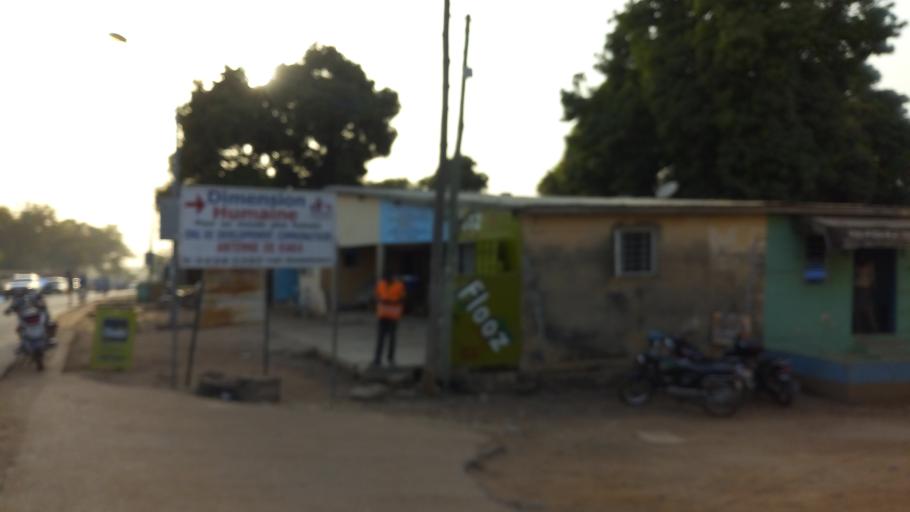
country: TG
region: Kara
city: Kara
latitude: 9.5513
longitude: 1.2025
